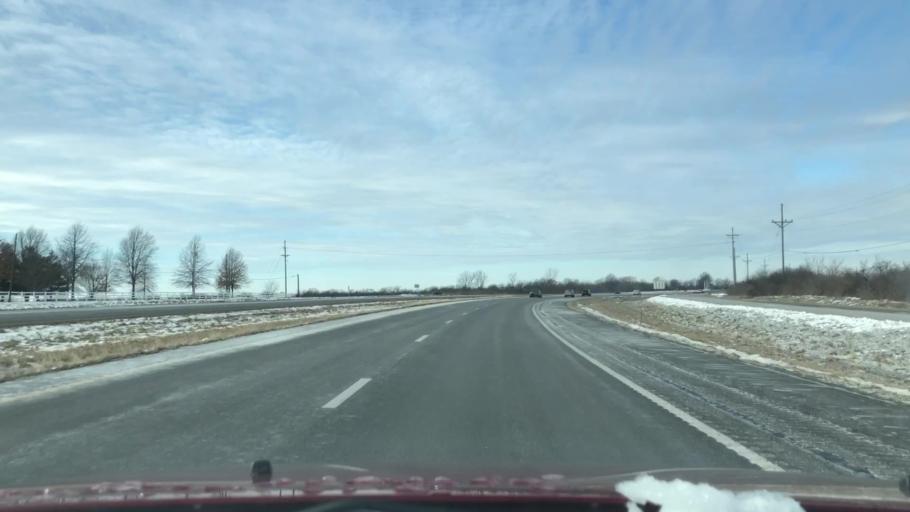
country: US
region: Missouri
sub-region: Jackson County
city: Lake Lotawana
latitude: 38.8935
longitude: -94.2819
